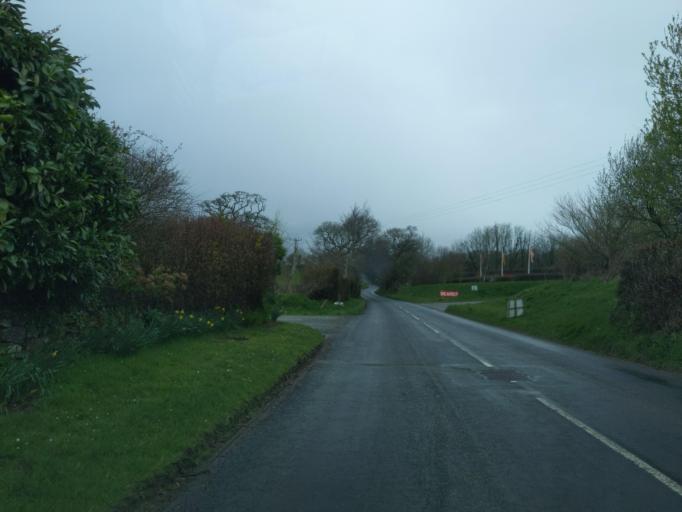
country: GB
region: England
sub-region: Cornwall
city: North Hill
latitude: 50.5681
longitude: -4.4110
